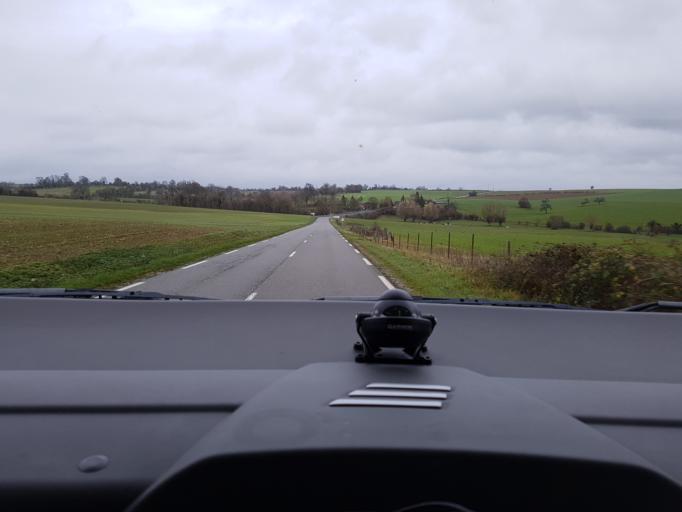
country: FR
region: Picardie
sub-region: Departement de l'Oise
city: Saint-Germer-de-Fly
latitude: 49.5032
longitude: 1.7856
